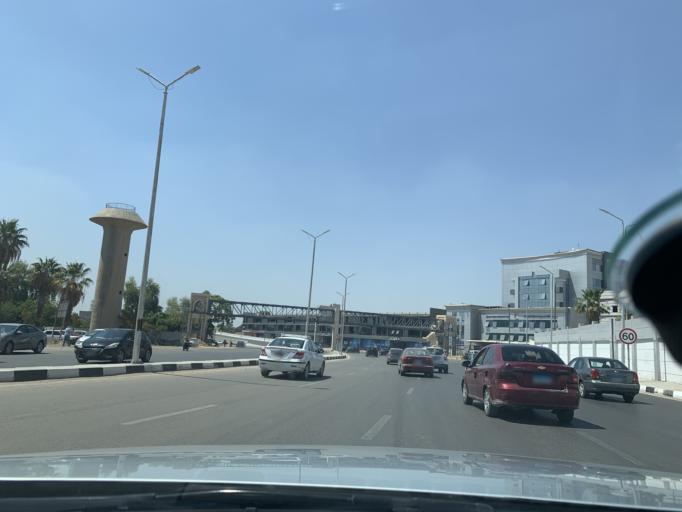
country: EG
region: Muhafazat al Qahirah
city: Cairo
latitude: 30.0906
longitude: 31.3487
